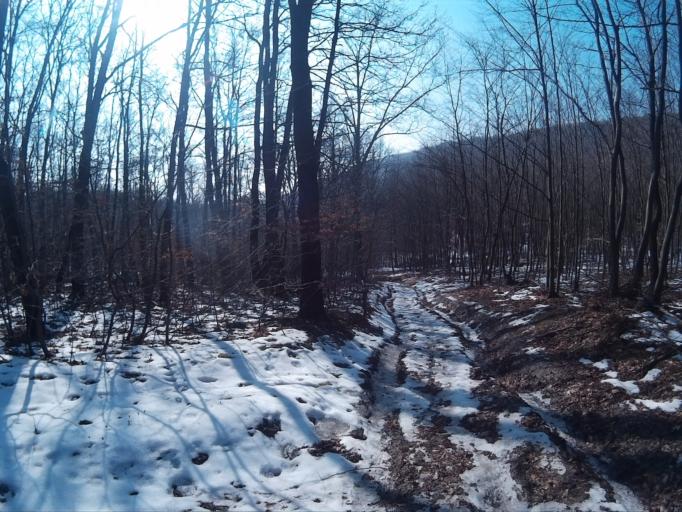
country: HU
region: Nograd
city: Paszto
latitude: 47.9848
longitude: 19.6823
